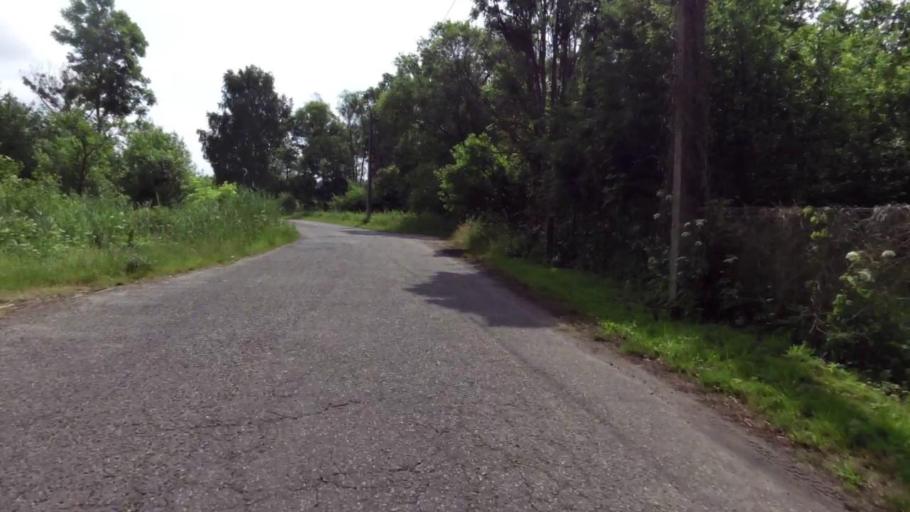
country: PL
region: West Pomeranian Voivodeship
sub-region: Powiat kamienski
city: Wolin
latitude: 53.7640
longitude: 14.6535
